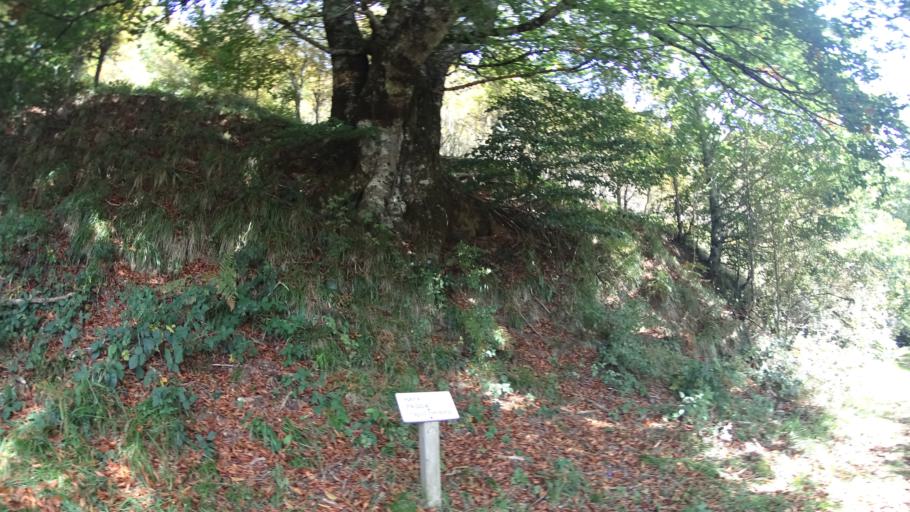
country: ES
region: Navarre
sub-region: Provincia de Navarra
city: Oronz
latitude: 42.9907
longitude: -1.1024
